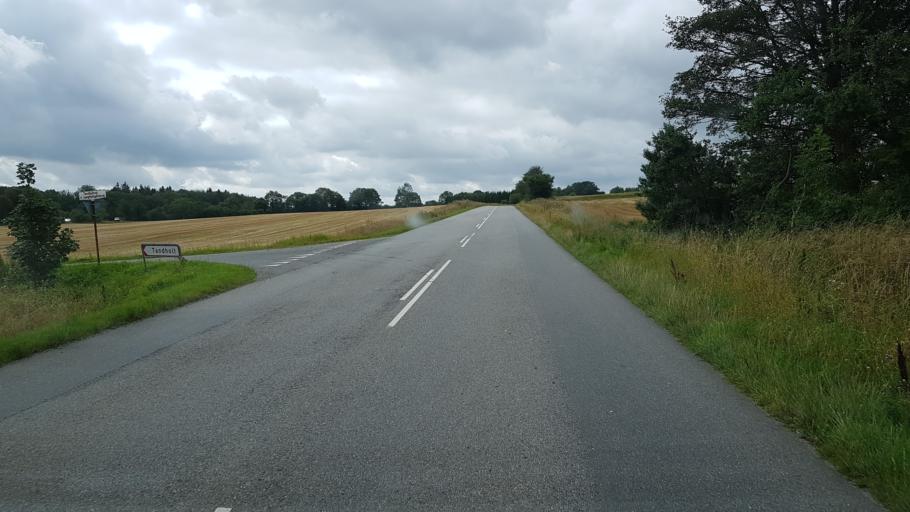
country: DK
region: South Denmark
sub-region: Kolding Kommune
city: Kolding
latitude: 55.4742
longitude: 9.4034
